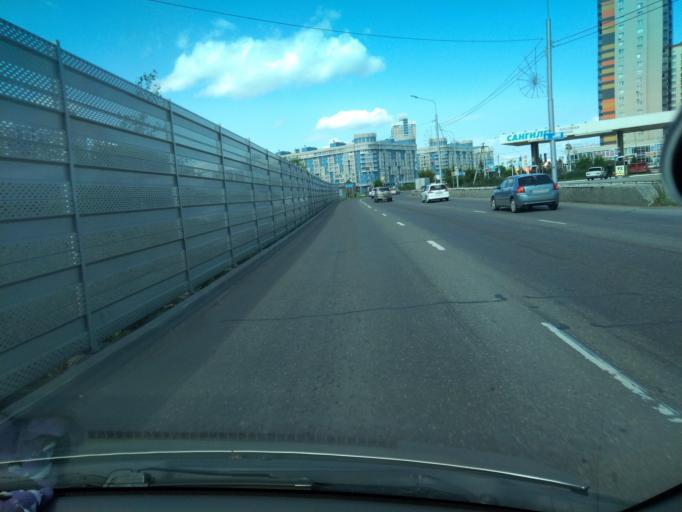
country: RU
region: Krasnoyarskiy
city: Krasnoyarsk
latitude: 56.0468
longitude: 92.9190
